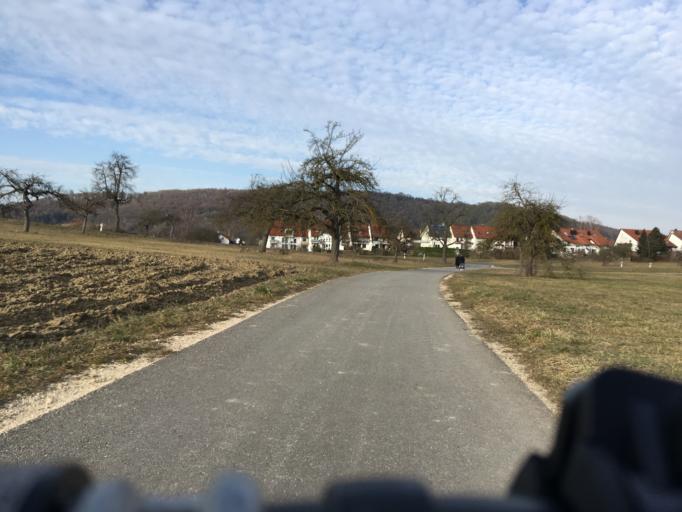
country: DE
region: Baden-Wuerttemberg
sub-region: Freiburg Region
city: Gottmadingen
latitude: 47.7314
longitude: 8.7661
